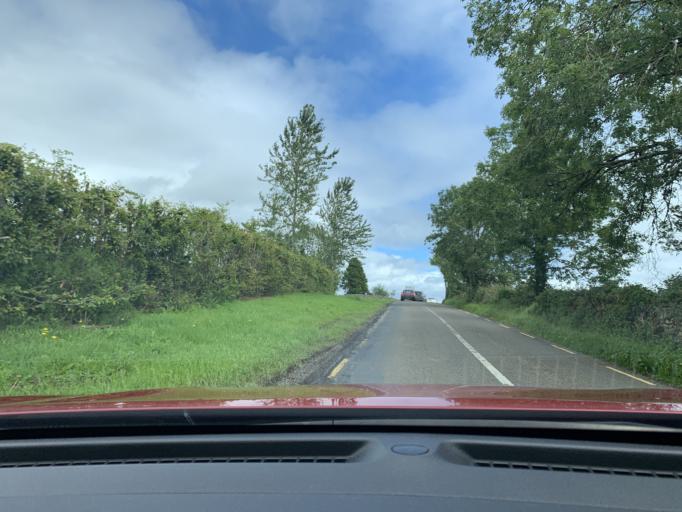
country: IE
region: Connaught
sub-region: County Leitrim
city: Carrick-on-Shannon
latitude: 53.9212
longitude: -8.1204
